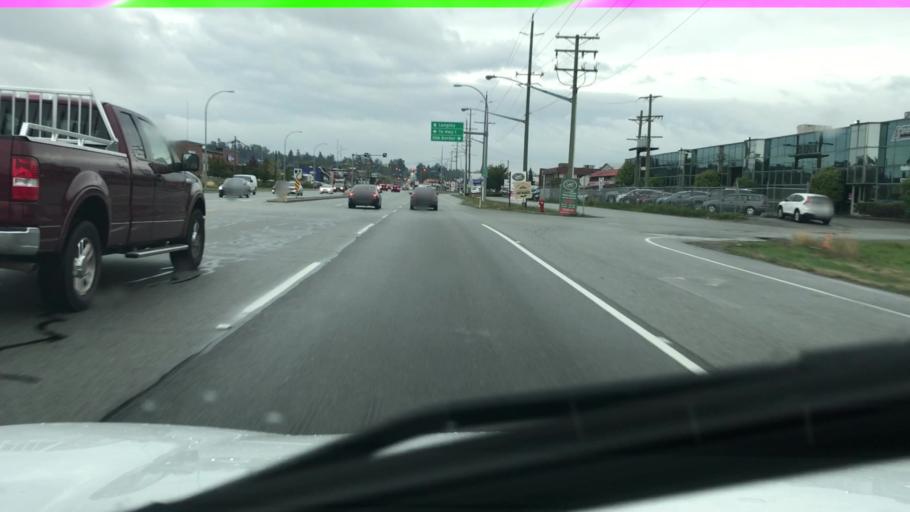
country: CA
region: British Columbia
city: Langley
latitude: 49.1040
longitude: -122.7419
